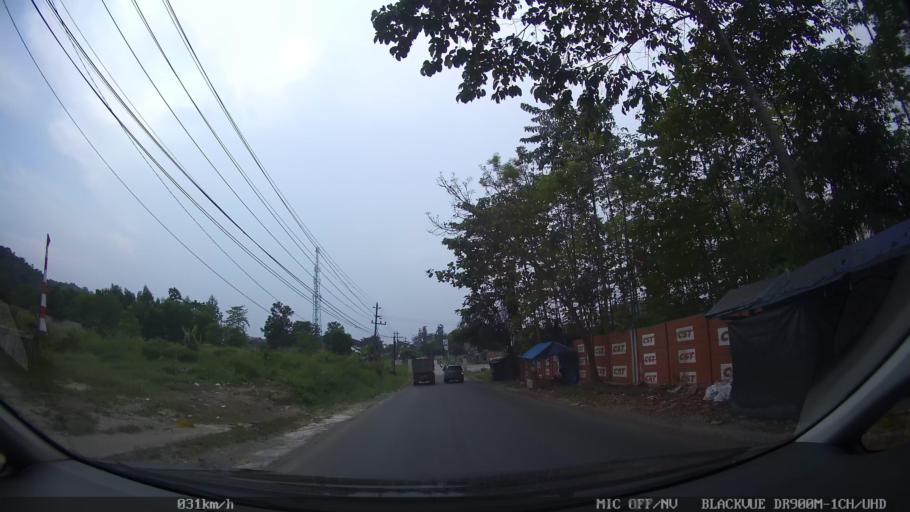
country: ID
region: Lampung
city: Panjang
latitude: -5.4180
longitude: 105.3283
